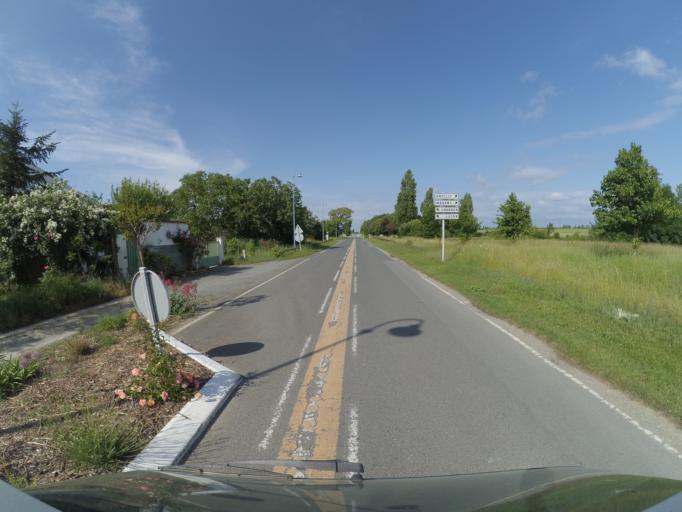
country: FR
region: Poitou-Charentes
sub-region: Departement de la Charente-Maritime
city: Andilly
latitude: 46.2456
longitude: -1.0627
